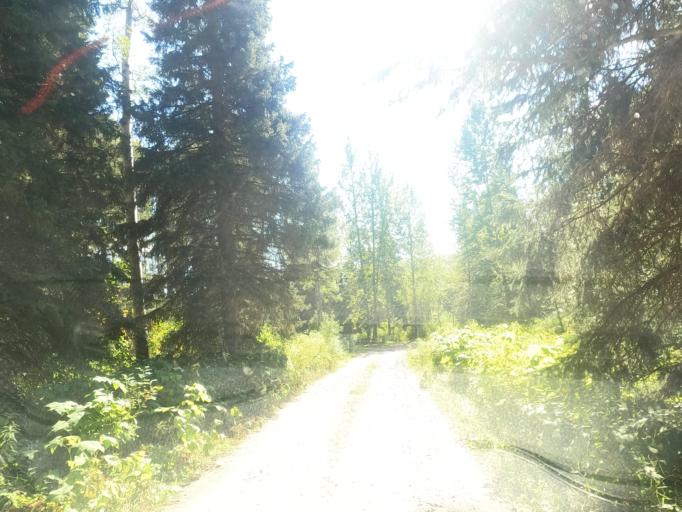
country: CA
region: British Columbia
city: Houston
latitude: 54.2860
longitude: -126.8517
